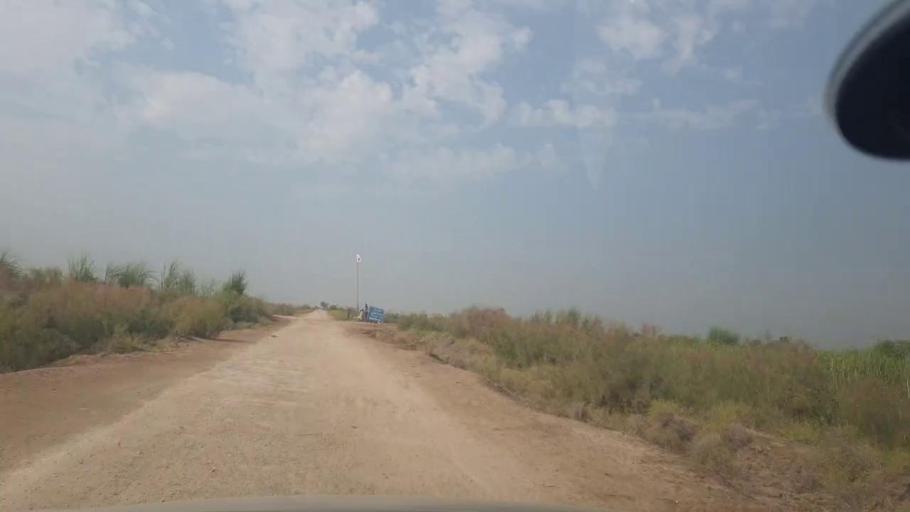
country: PK
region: Balochistan
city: Mehrabpur
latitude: 28.0201
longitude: 68.1377
